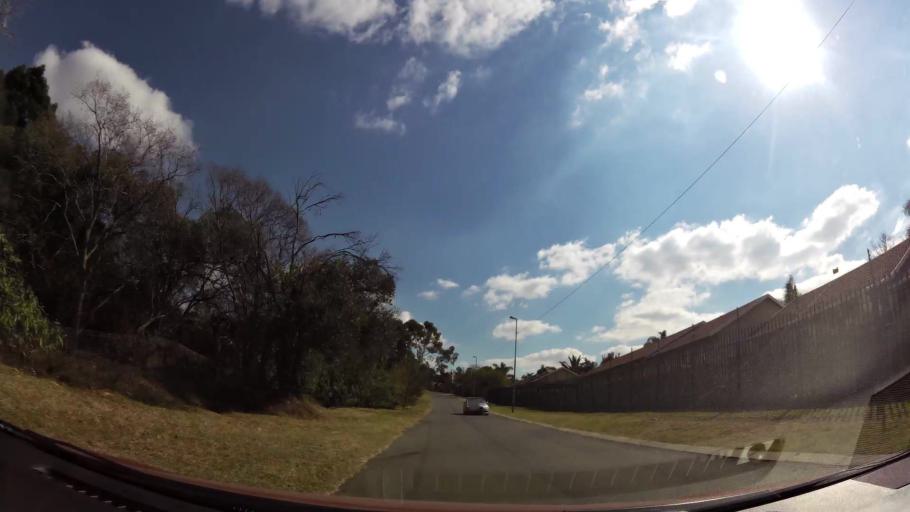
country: ZA
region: Gauteng
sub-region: West Rand District Municipality
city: Muldersdriseloop
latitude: -26.0662
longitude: 27.9578
